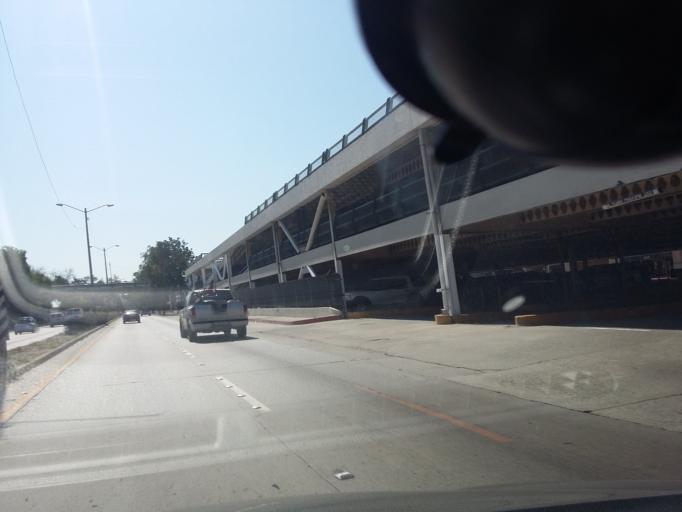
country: MX
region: Baja California
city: Tijuana
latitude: 32.5296
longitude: -117.0200
